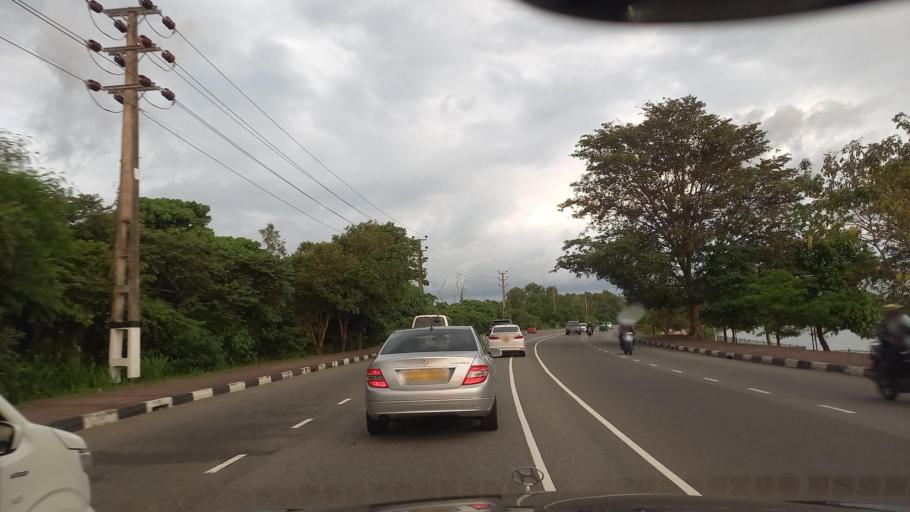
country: LK
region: Western
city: Battaramulla South
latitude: 6.8830
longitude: 79.9268
